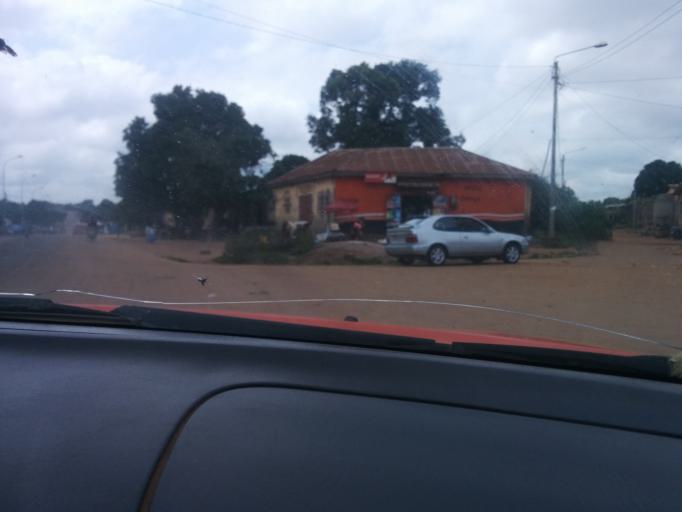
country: CI
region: Vallee du Bandama
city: Bouake
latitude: 7.6952
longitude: -5.0392
